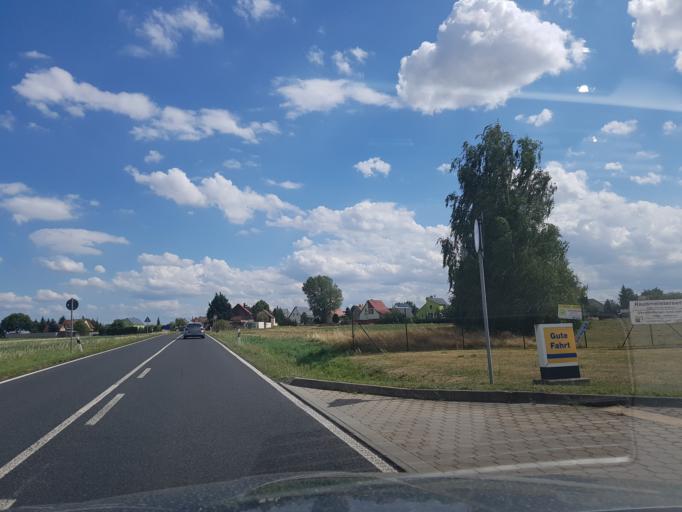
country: DE
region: Saxony
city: Grossenhain
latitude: 51.2686
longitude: 13.5355
